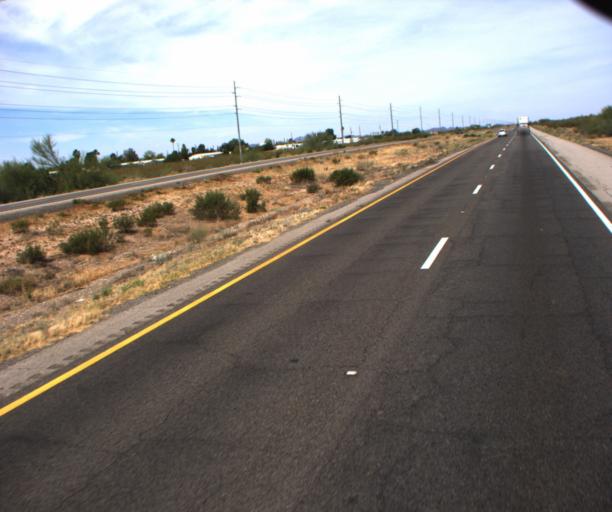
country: US
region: Arizona
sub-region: Maricopa County
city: Sun City West
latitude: 33.7861
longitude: -112.5389
